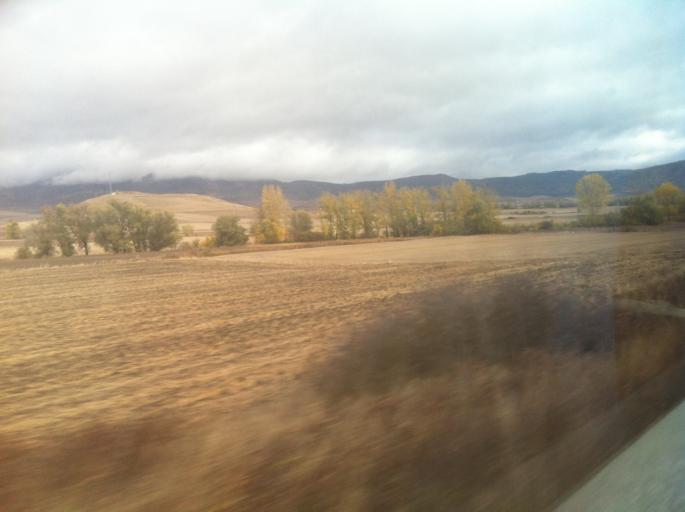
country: ES
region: Castille and Leon
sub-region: Provincia de Burgos
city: Cubo de Bureba
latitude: 42.6247
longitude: -3.1977
